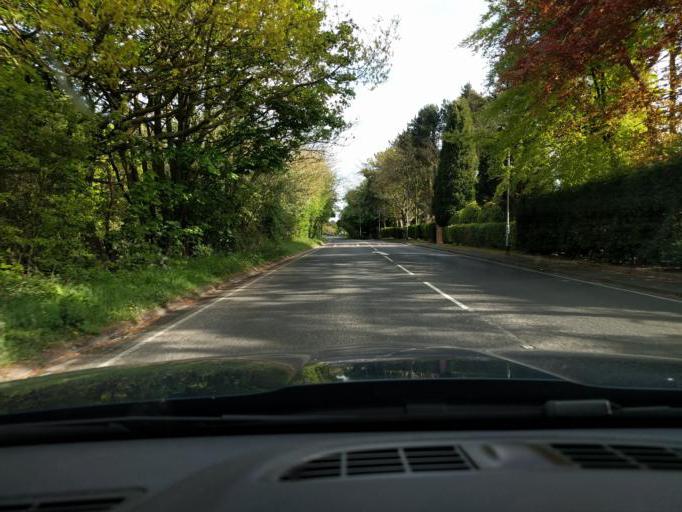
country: GB
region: England
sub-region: Northumberland
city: Pegswood
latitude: 55.1471
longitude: -1.6575
